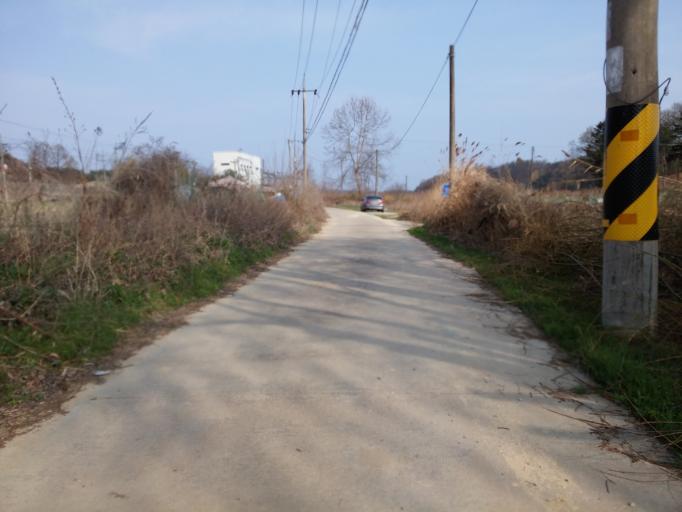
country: KR
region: Daejeon
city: Sintansin
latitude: 36.4950
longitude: 127.3950
